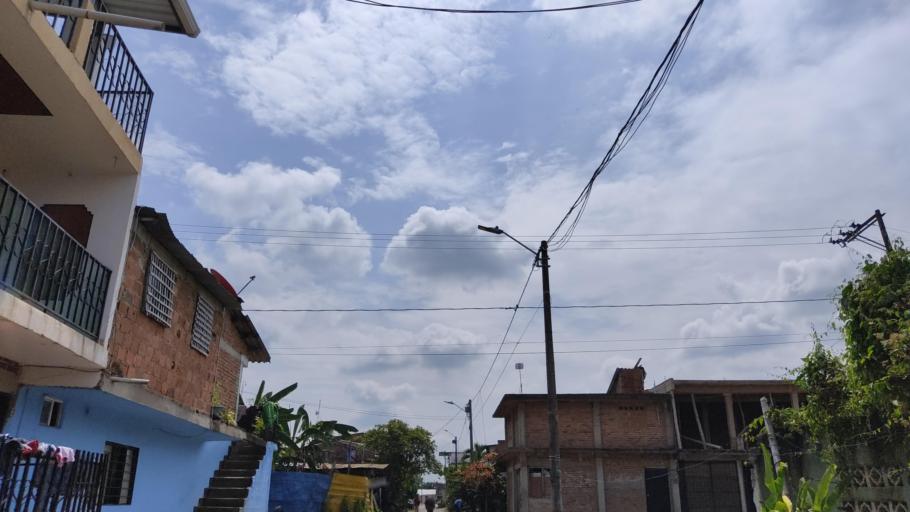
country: CO
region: Cauca
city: Buenos Aires
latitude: 3.1263
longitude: -76.5920
